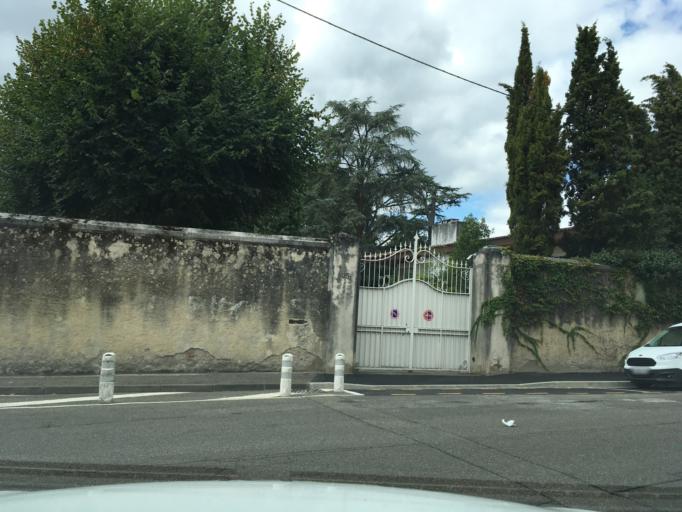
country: FR
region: Aquitaine
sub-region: Departement du Lot-et-Garonne
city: Le Passage
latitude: 44.1972
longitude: 0.6171
